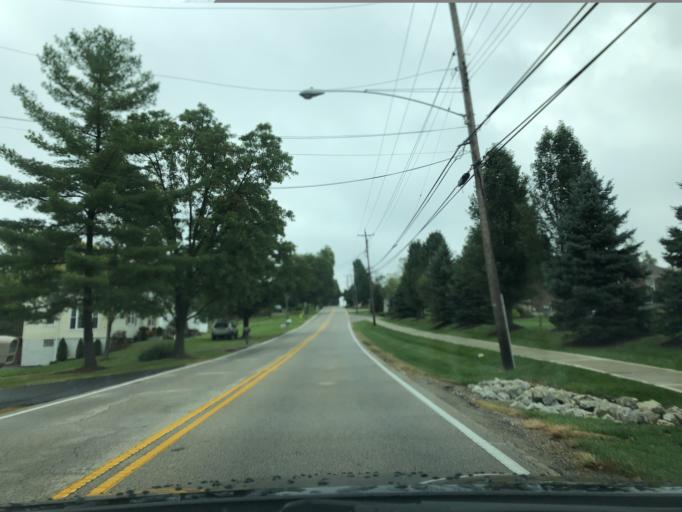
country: US
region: Ohio
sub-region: Hamilton County
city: Highpoint
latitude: 39.2852
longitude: -84.3819
